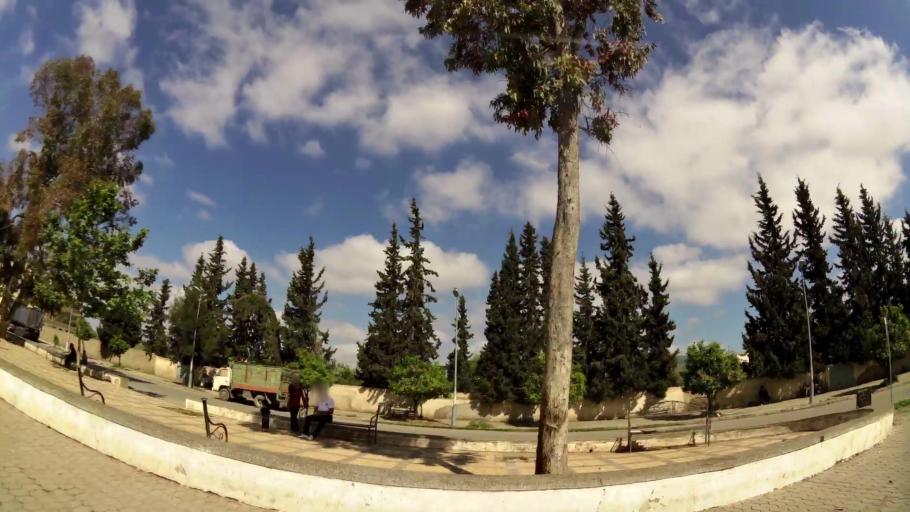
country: MA
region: Fes-Boulemane
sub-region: Fes
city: Fes
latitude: 34.0354
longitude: -5.0250
